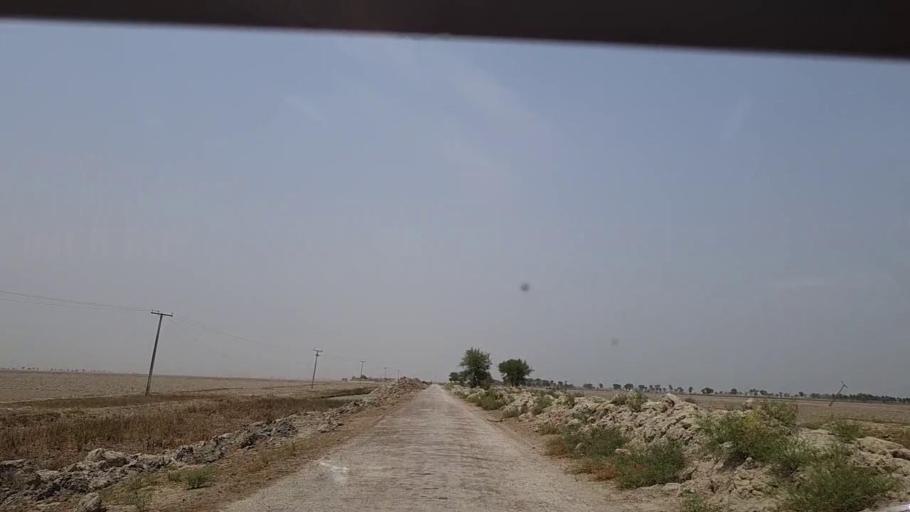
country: PK
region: Sindh
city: Khairpur Nathan Shah
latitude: 27.0343
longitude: 67.6194
